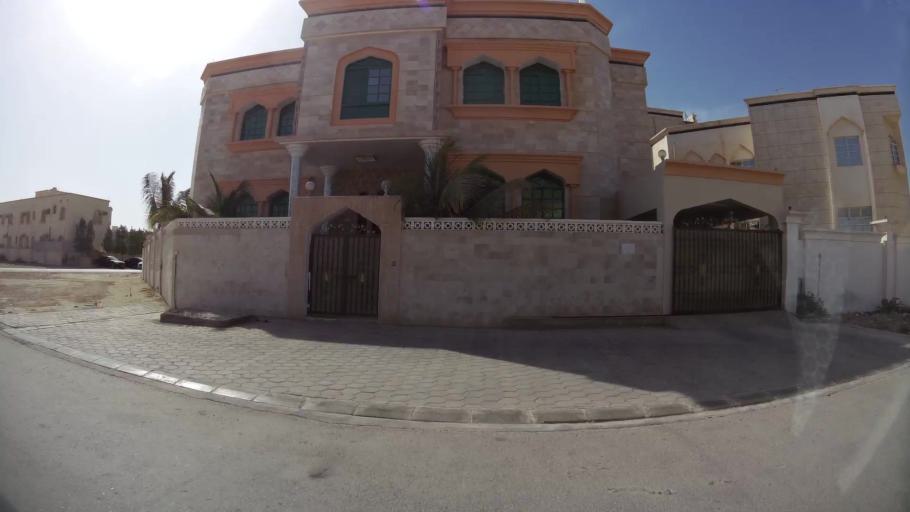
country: OM
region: Zufar
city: Salalah
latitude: 17.0051
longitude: 54.0081
